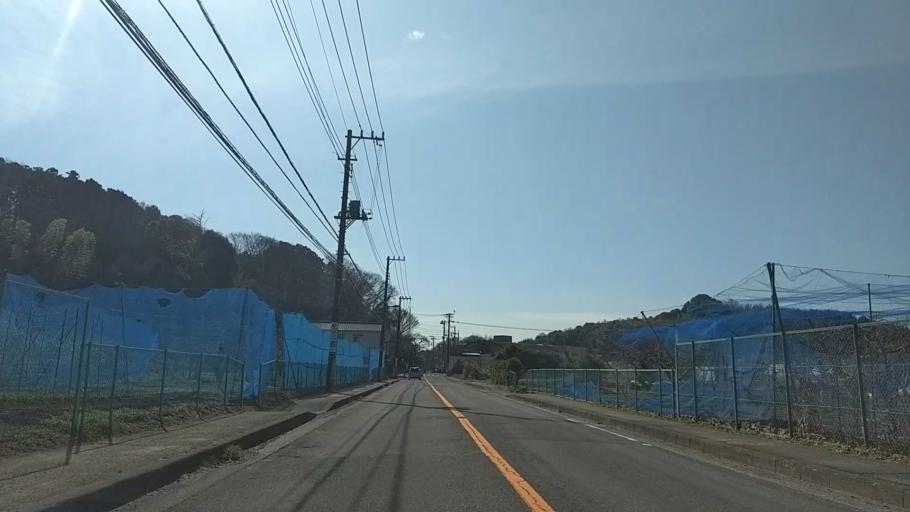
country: JP
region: Kanagawa
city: Kamakura
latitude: 35.4054
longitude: 139.5531
